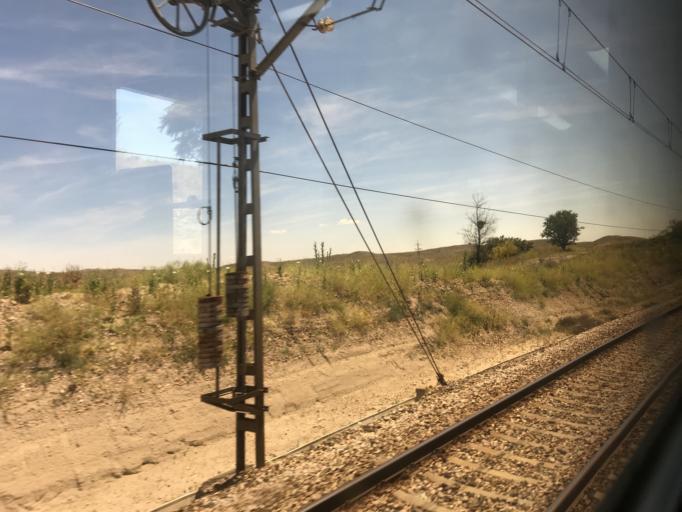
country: ES
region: Madrid
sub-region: Provincia de Madrid
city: Ciempozuelos
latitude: 40.1840
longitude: -3.6393
